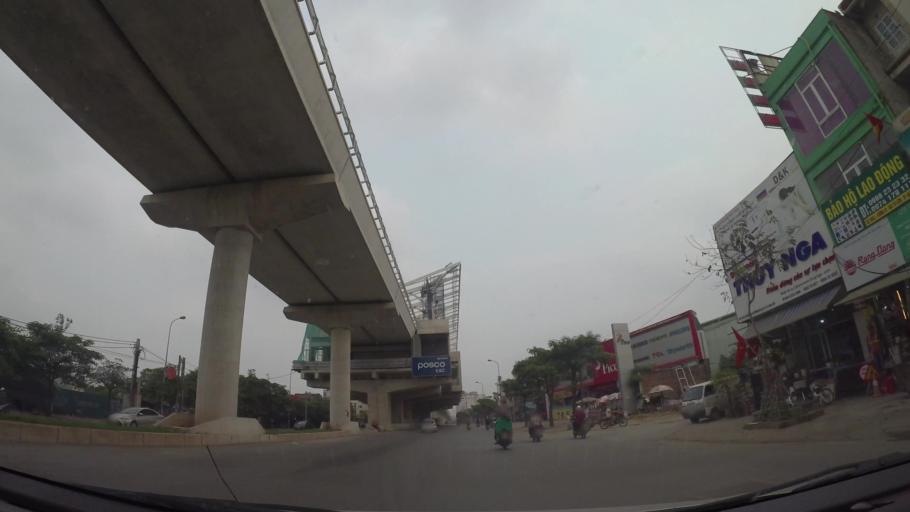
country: VN
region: Ha Noi
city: Cau Dien
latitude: 21.0482
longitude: 105.7439
